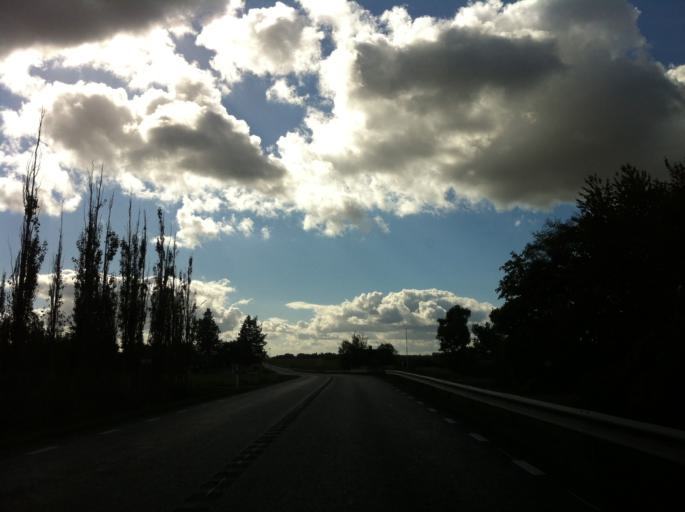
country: SE
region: Skane
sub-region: Tomelilla Kommun
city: Tomelilla
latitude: 55.6466
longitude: 14.0123
